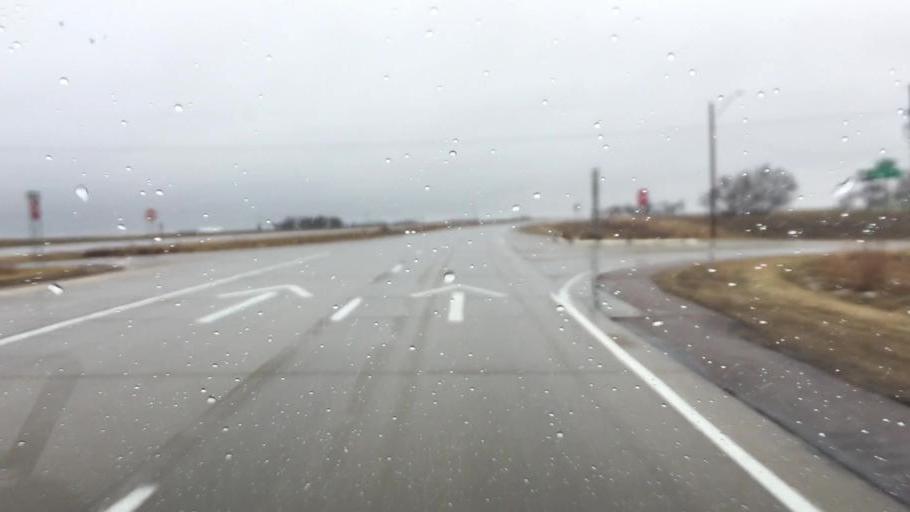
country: US
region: Iowa
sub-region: O'Brien County
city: Sheldon
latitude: 43.0695
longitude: -95.8969
